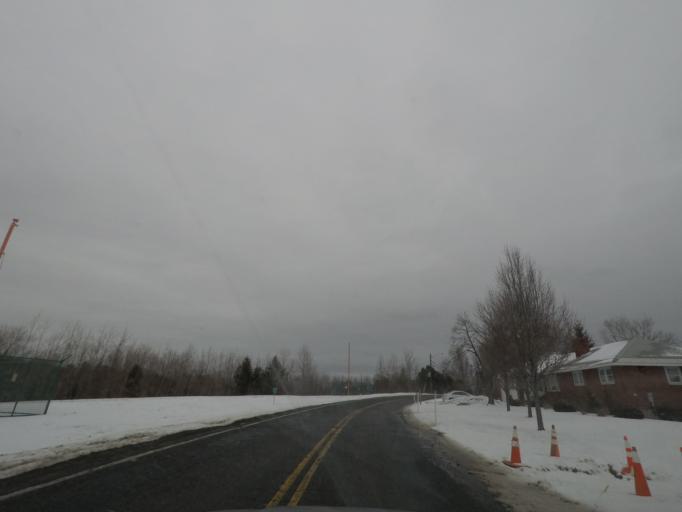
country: US
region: New York
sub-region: Schenectady County
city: Niskayuna
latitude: 42.7659
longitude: -73.8051
